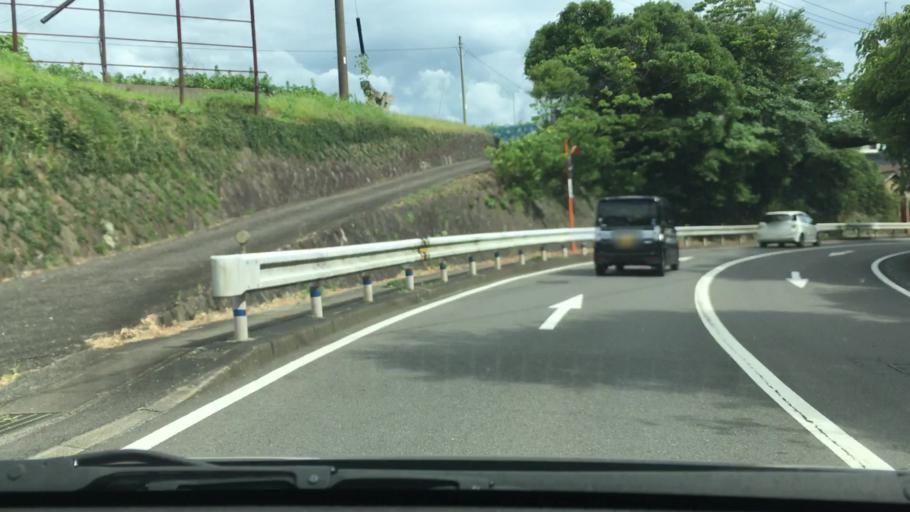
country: JP
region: Nagasaki
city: Togitsu
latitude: 32.9165
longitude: 129.7873
